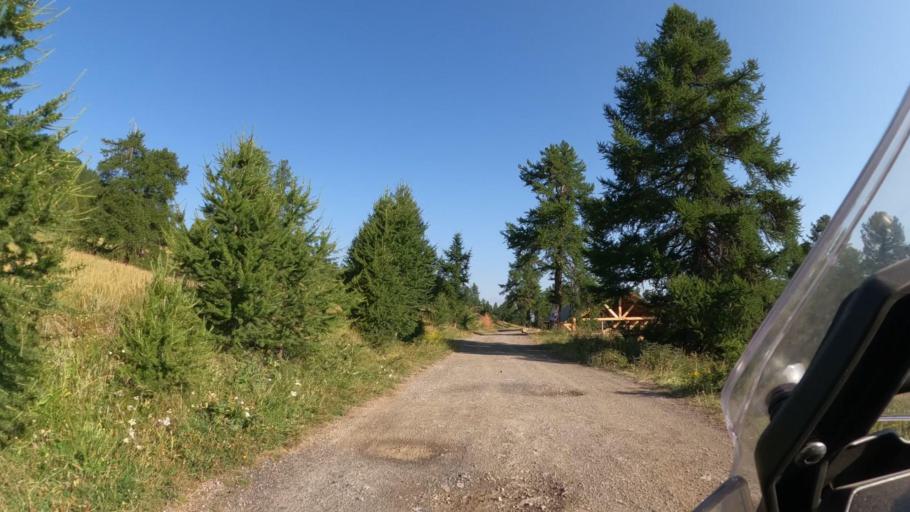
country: FR
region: Provence-Alpes-Cote d'Azur
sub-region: Departement des Hautes-Alpes
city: Guillestre
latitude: 44.6101
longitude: 6.6676
